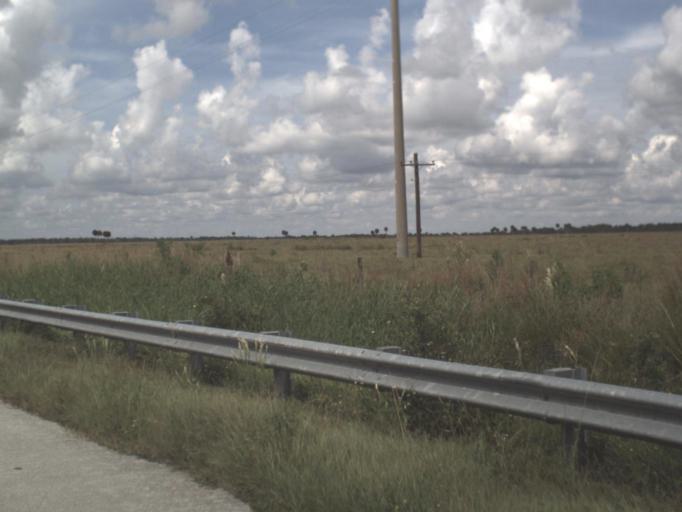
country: US
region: Florida
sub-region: Okeechobee County
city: Okeechobee
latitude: 27.2436
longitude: -80.9195
